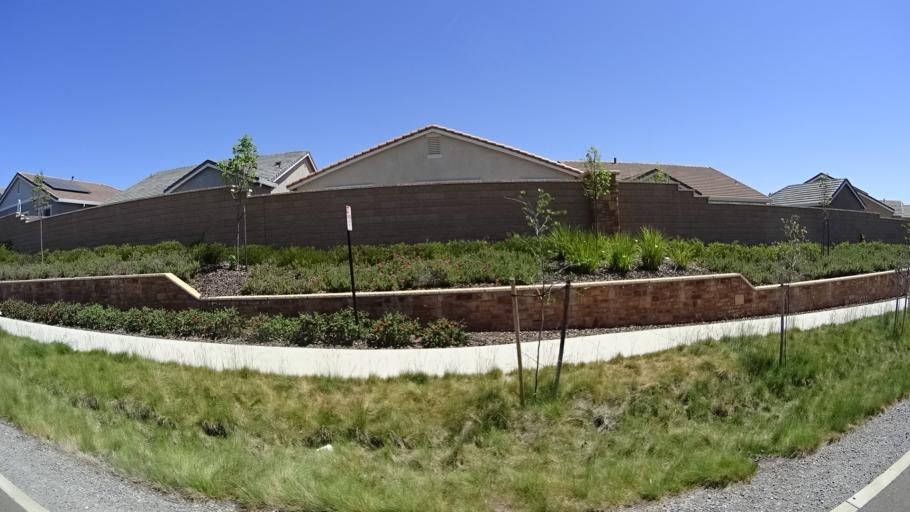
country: US
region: California
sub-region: Placer County
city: Rocklin
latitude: 38.8268
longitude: -121.2671
